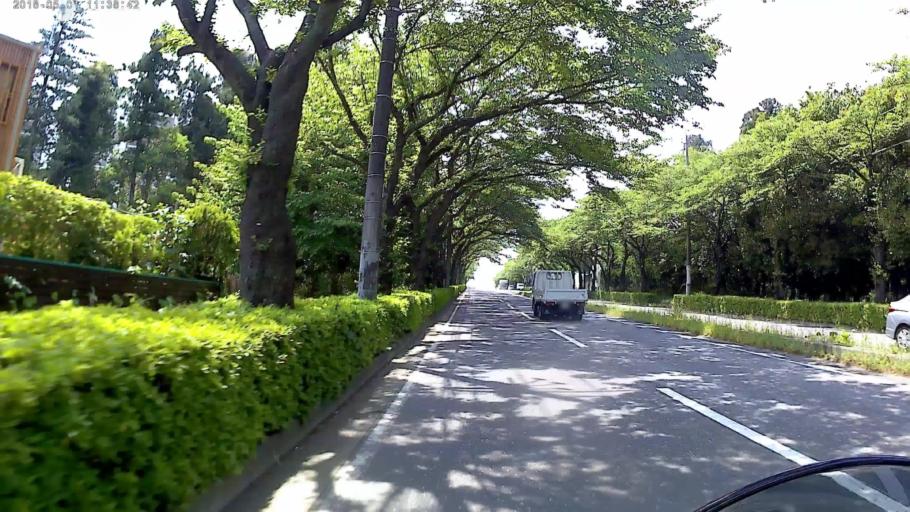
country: JP
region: Kanagawa
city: Minami-rinkan
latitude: 35.5073
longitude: 139.4912
